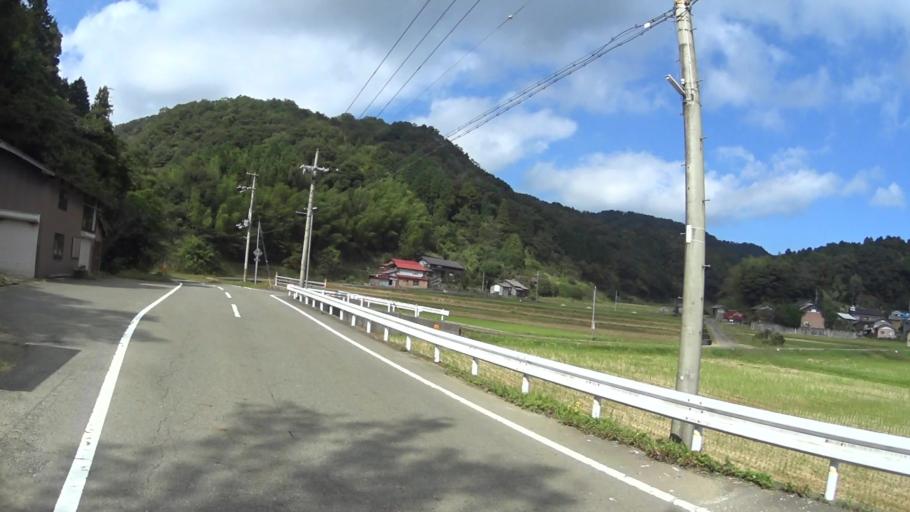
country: JP
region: Kyoto
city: Miyazu
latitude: 35.6825
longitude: 135.2667
